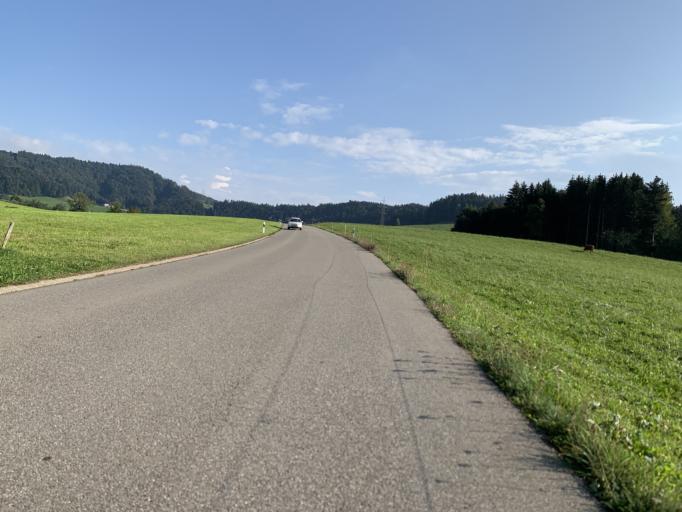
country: CH
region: Zurich
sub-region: Bezirk Hinwil
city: Baretswil
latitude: 47.3293
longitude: 8.8639
